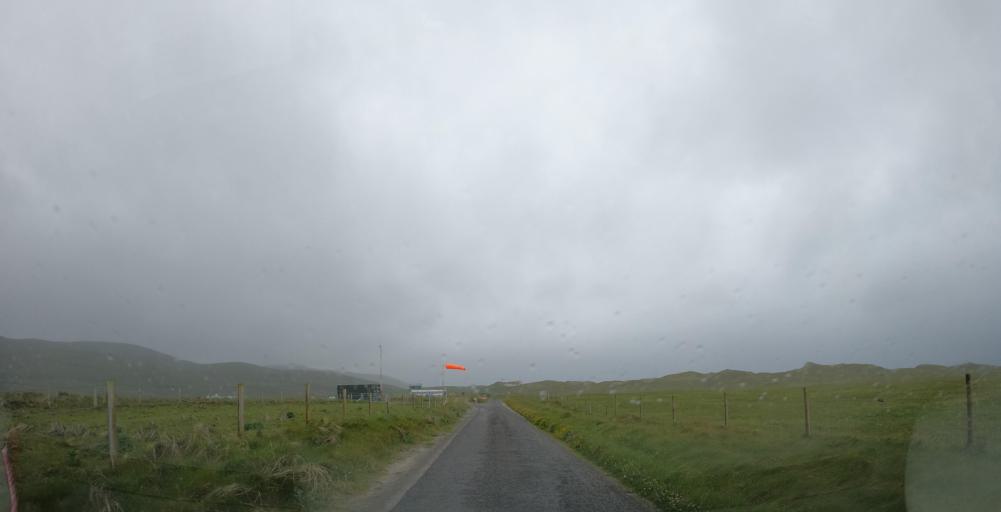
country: GB
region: Scotland
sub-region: Eilean Siar
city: Barra
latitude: 57.0266
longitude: -7.4459
